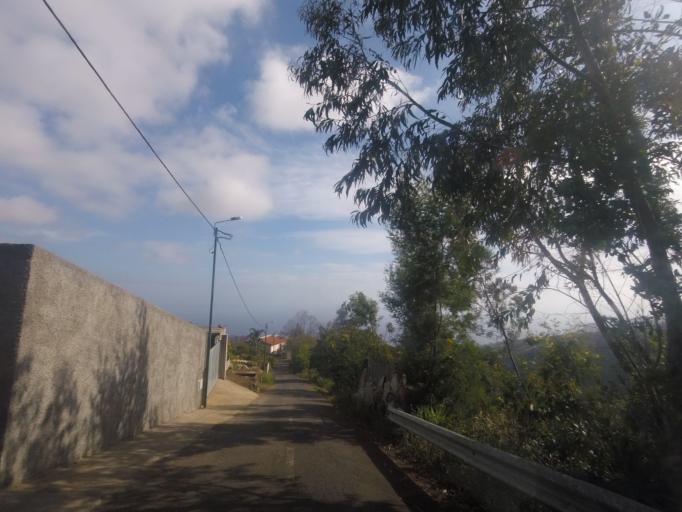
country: PT
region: Madeira
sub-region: Camara de Lobos
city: Curral das Freiras
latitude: 32.6798
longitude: -16.9533
